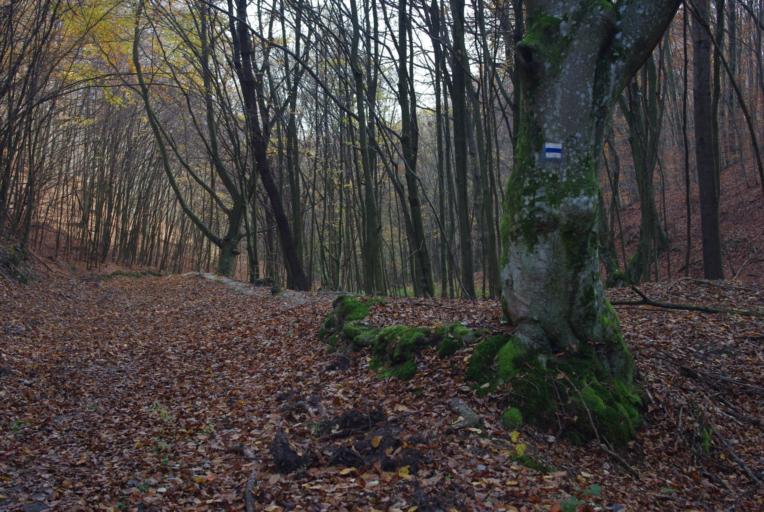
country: HU
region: Borsod-Abauj-Zemplen
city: Sarospatak
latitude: 48.4310
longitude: 21.5085
